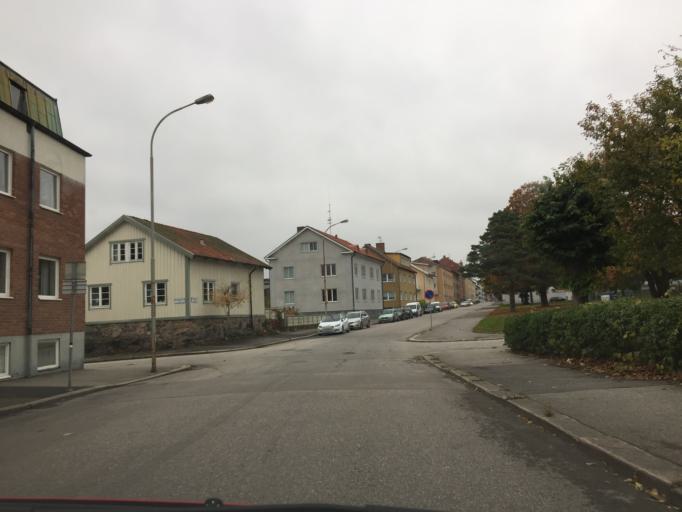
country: SE
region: Vaestra Goetaland
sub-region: Trollhattan
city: Trollhattan
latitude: 58.2769
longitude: 12.2819
